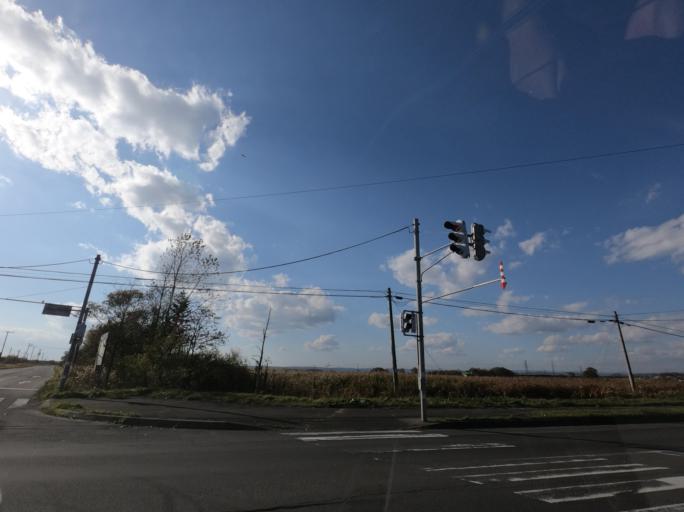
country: JP
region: Hokkaido
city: Kushiro
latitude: 43.0382
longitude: 144.3144
